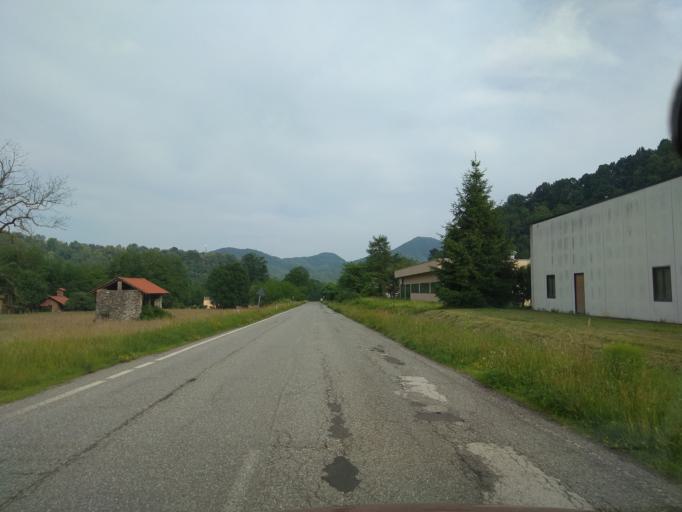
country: IT
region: Piedmont
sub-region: Provincia di Biella
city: Coggiola
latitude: 45.6806
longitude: 8.1911
